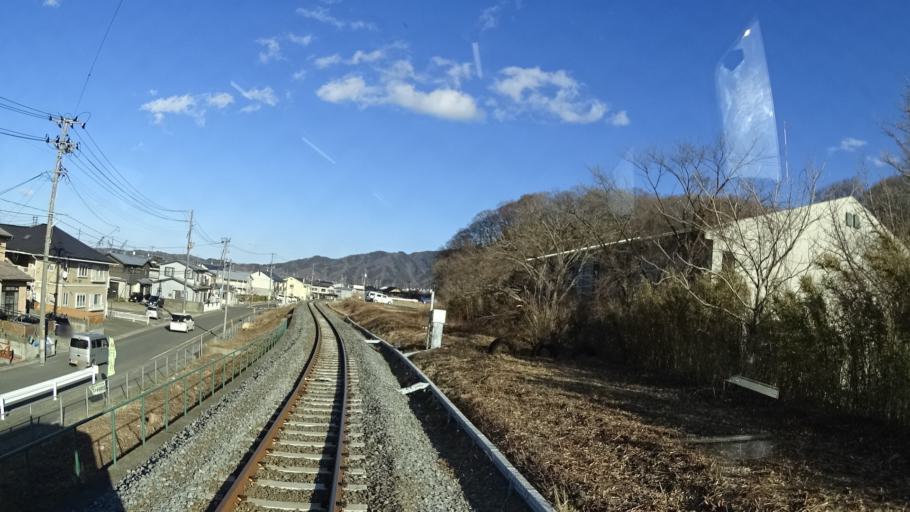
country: JP
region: Iwate
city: Miyako
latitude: 39.6372
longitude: 141.9572
